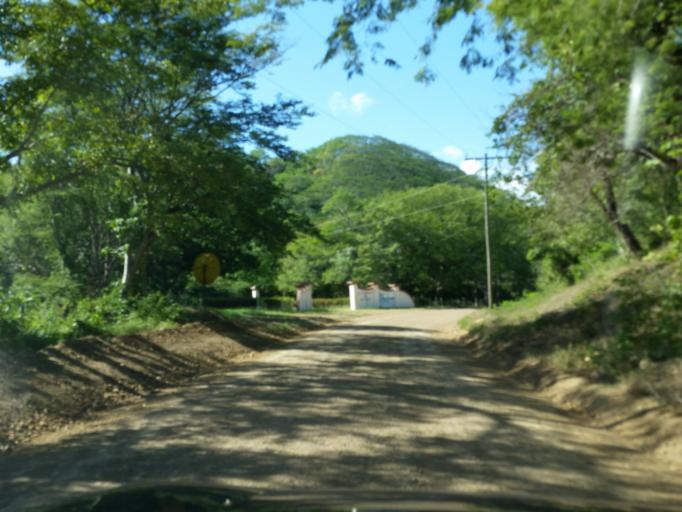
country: NI
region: Rivas
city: San Juan del Sur
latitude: 11.1900
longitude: -85.8104
